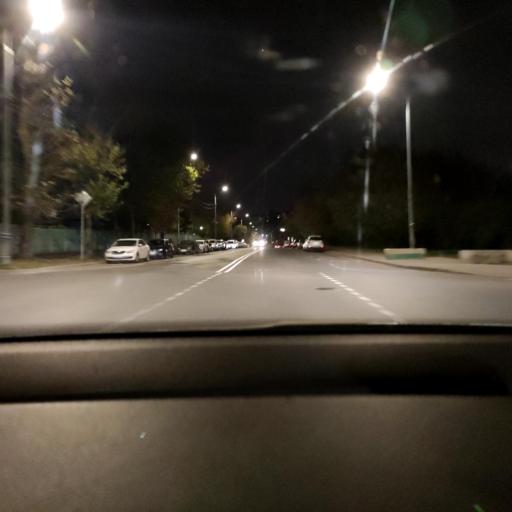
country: RU
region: Moscow
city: Vagonoremont
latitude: 55.8994
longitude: 37.5299
